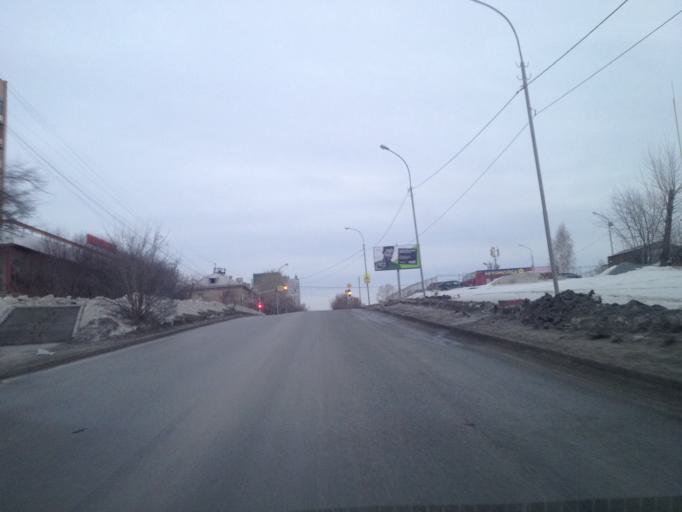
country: RU
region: Sverdlovsk
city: Sovkhoznyy
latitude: 56.7574
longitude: 60.6104
